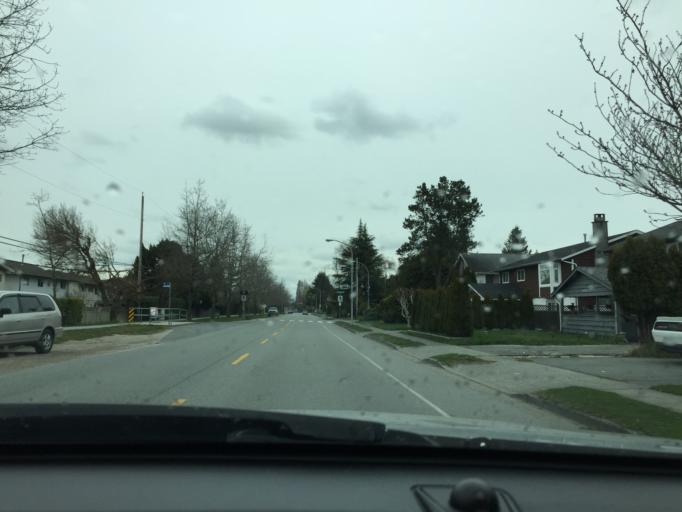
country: CA
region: British Columbia
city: Richmond
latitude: 49.1446
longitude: -123.1251
